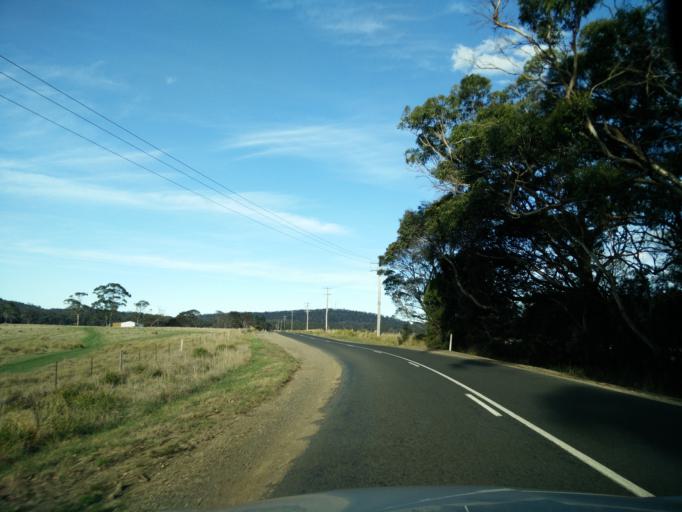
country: AU
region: Tasmania
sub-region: Break O'Day
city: St Helens
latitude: -41.8950
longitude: 148.2596
